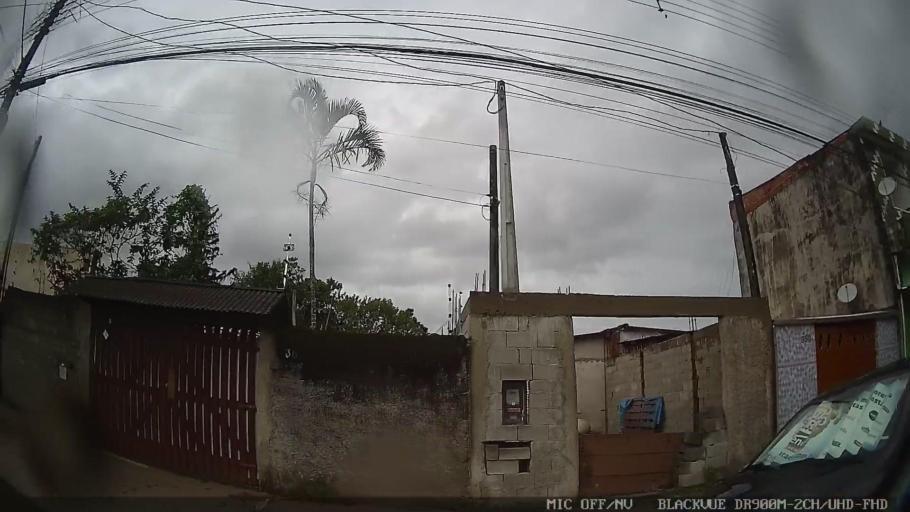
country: BR
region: Sao Paulo
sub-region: Itanhaem
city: Itanhaem
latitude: -24.1641
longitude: -46.7904
